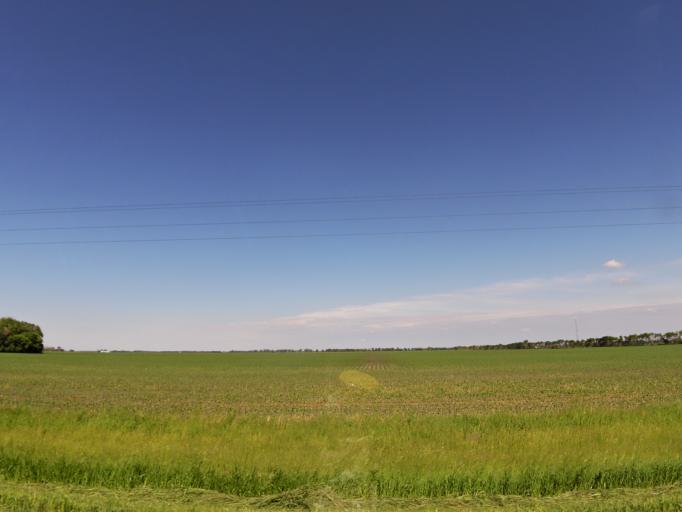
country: US
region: North Dakota
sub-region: Walsh County
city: Grafton
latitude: 48.3049
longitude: -97.2550
